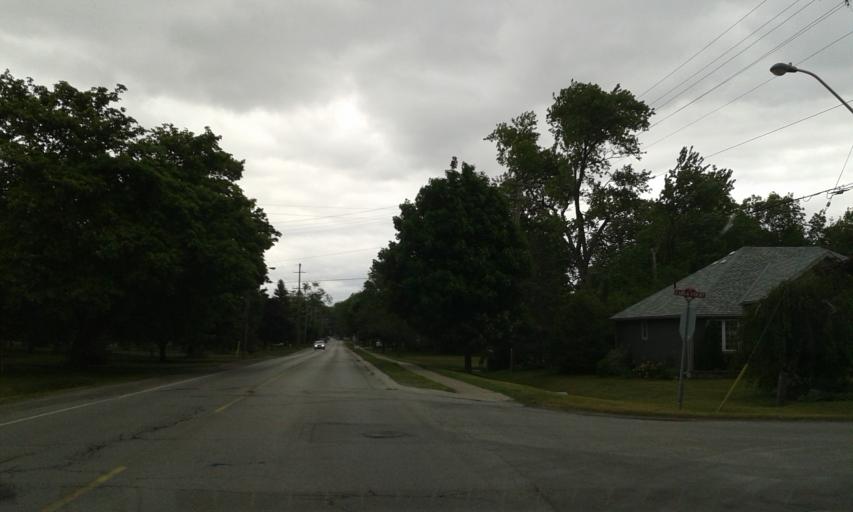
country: CA
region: Ontario
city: Prince Edward
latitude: 43.9495
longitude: -77.3623
